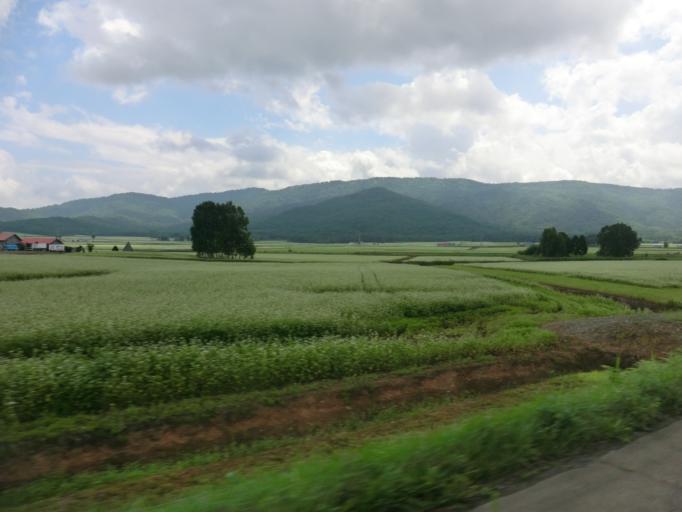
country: JP
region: Hokkaido
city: Fukagawa
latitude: 43.9541
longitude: 142.1568
